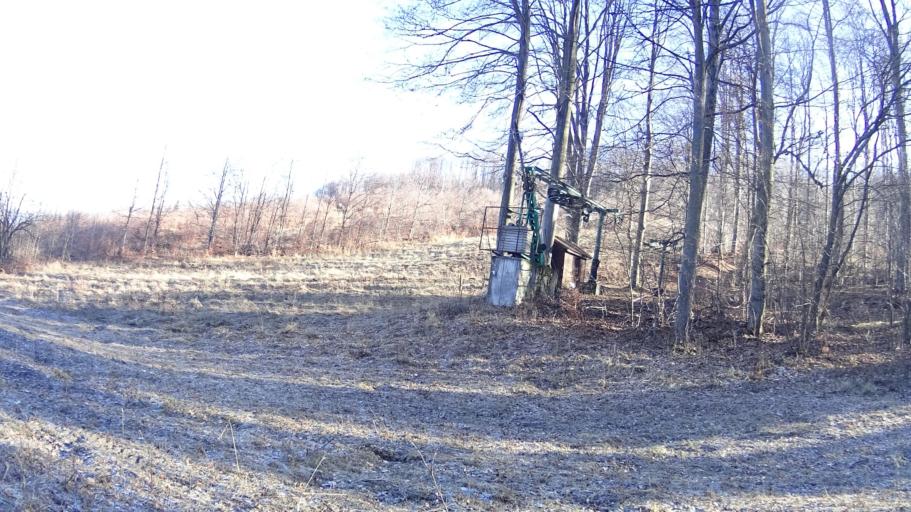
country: HU
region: Heves
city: Szilvasvarad
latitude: 48.1004
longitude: 20.4848
